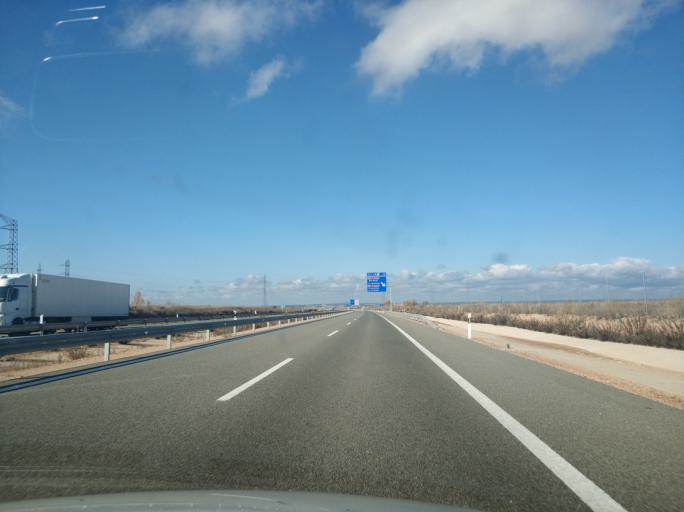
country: ES
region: Castille and Leon
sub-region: Provincia de Soria
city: Frechilla de Almazan
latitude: 41.4378
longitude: -2.4998
